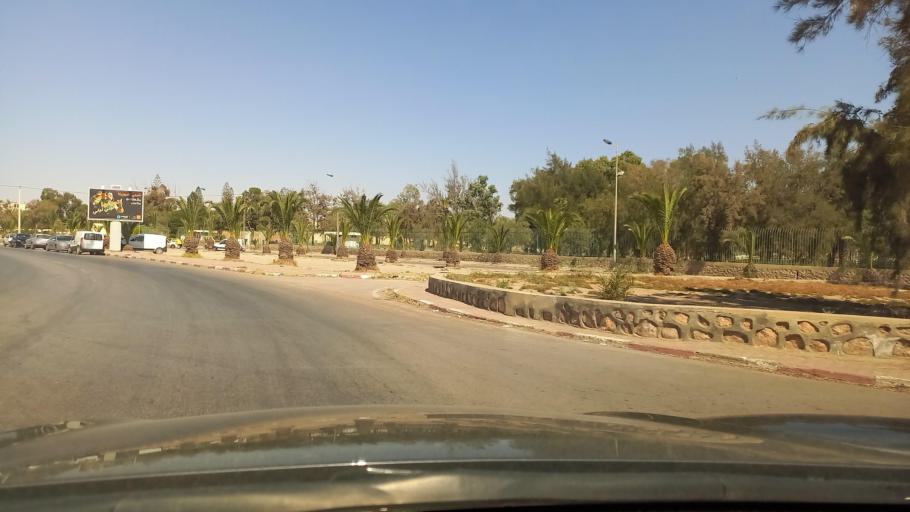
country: TN
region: Safaqis
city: Sfax
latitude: 34.7330
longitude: 10.7438
